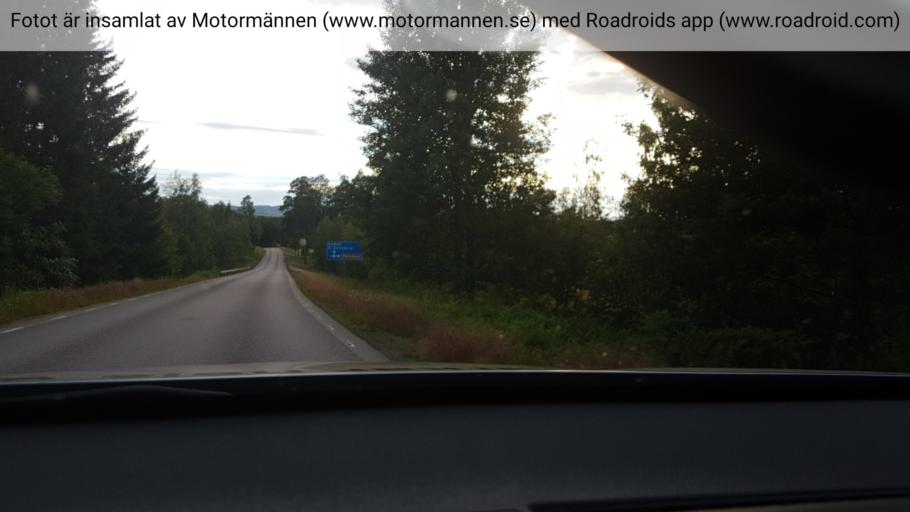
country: SE
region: Vaermland
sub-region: Sunne Kommun
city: Sunne
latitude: 59.7577
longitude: 13.2480
